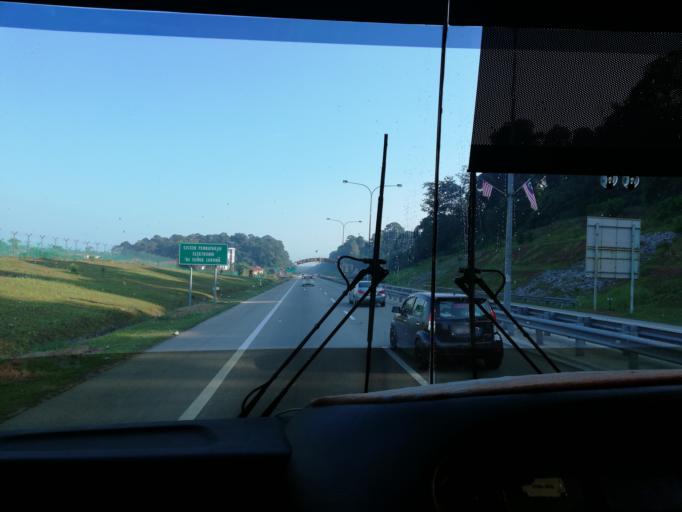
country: MY
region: Negeri Sembilan
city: Port Dickson
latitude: 2.5021
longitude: 101.8654
